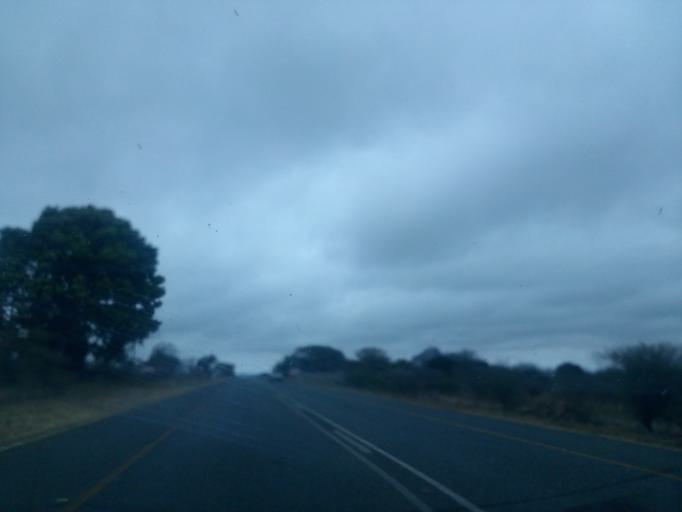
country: ZA
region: Limpopo
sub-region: Vhembe District Municipality
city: Louis Trichardt
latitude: -23.0883
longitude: 29.9053
